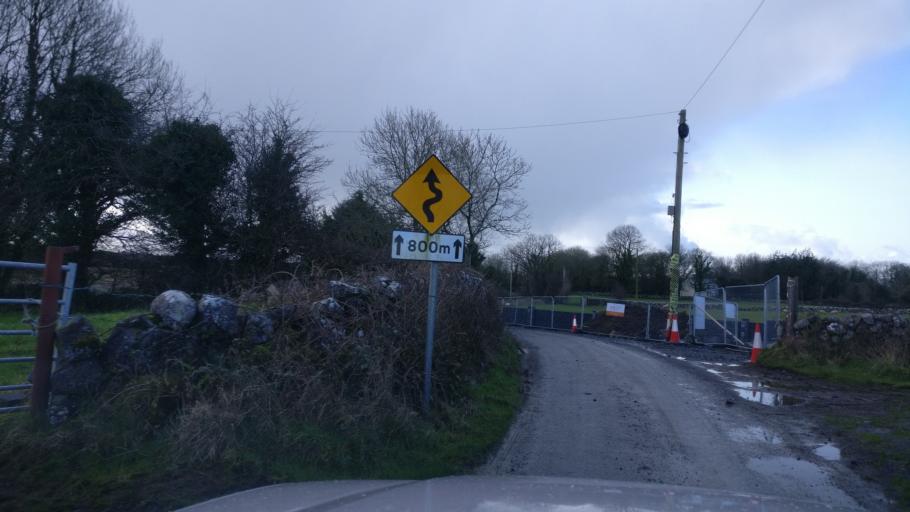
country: IE
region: Connaught
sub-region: County Galway
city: Oranmore
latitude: 53.2631
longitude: -8.8837
